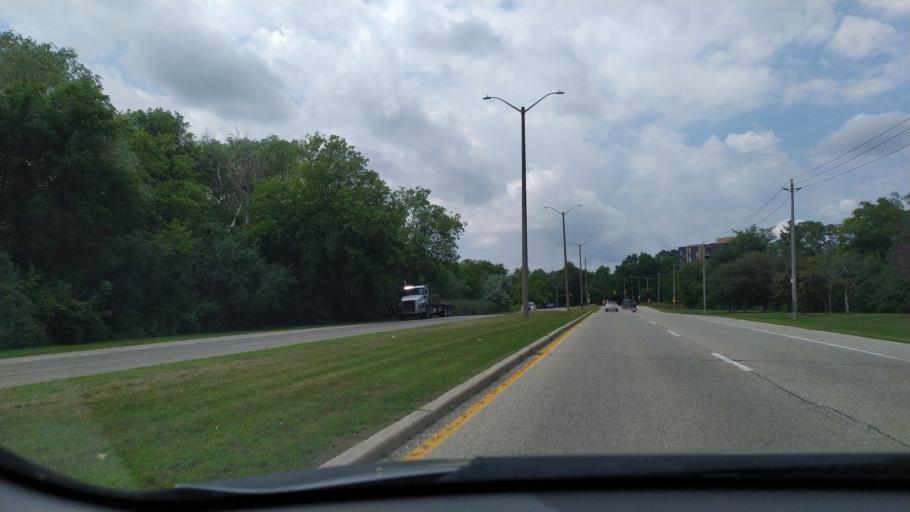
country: CA
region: Ontario
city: Kitchener
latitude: 43.4306
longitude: -80.4932
